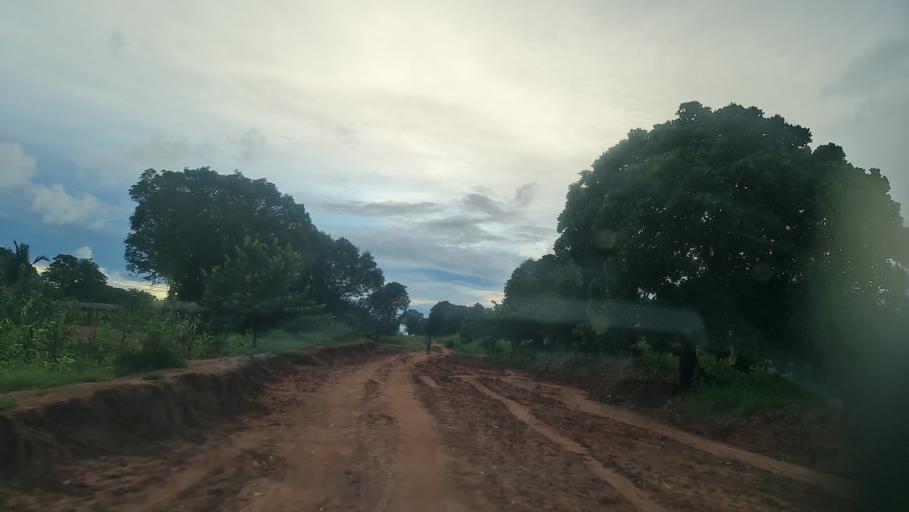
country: MZ
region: Nampula
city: Nacala
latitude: -14.7405
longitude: 39.9402
